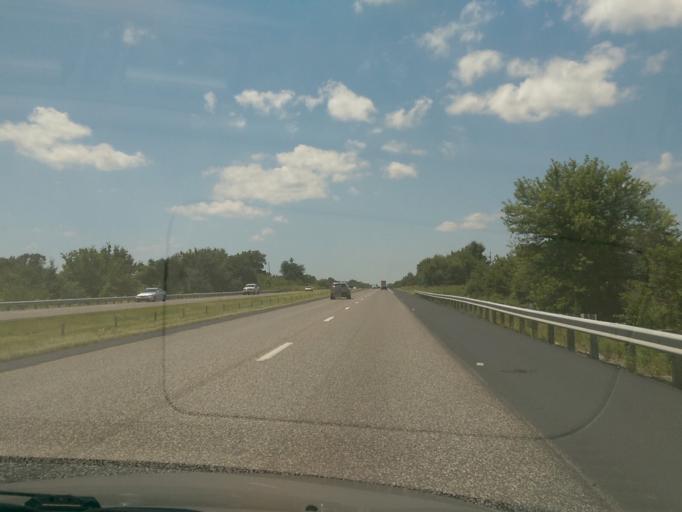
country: US
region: Missouri
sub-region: Cooper County
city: Boonville
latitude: 38.9391
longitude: -92.6312
